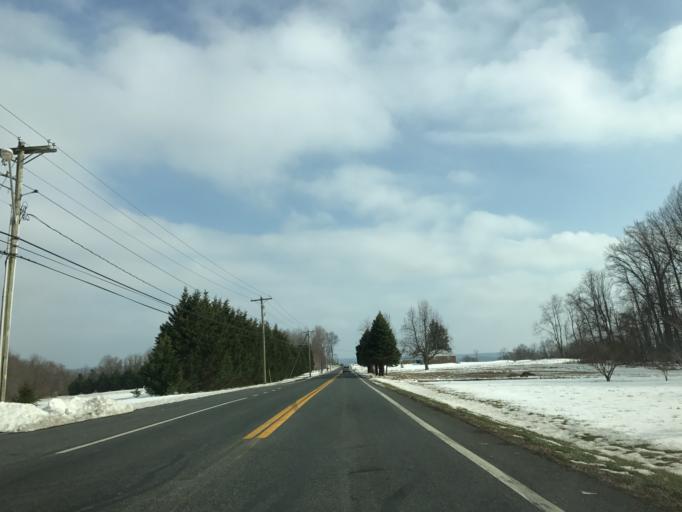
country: US
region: Maryland
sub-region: Harford County
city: South Bel Air
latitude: 39.6271
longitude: -76.2625
